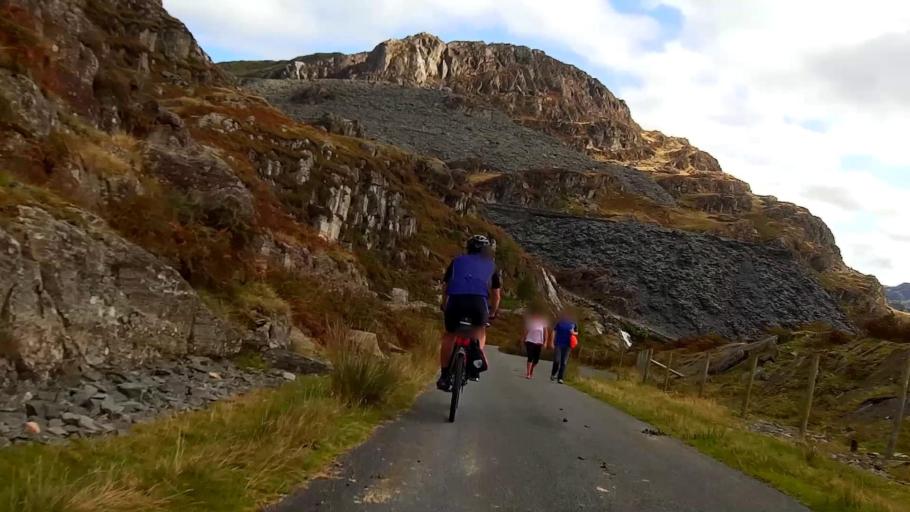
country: GB
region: Wales
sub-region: Gwynedd
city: Blaenau-Ffestiniog
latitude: 52.9889
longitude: -3.9687
